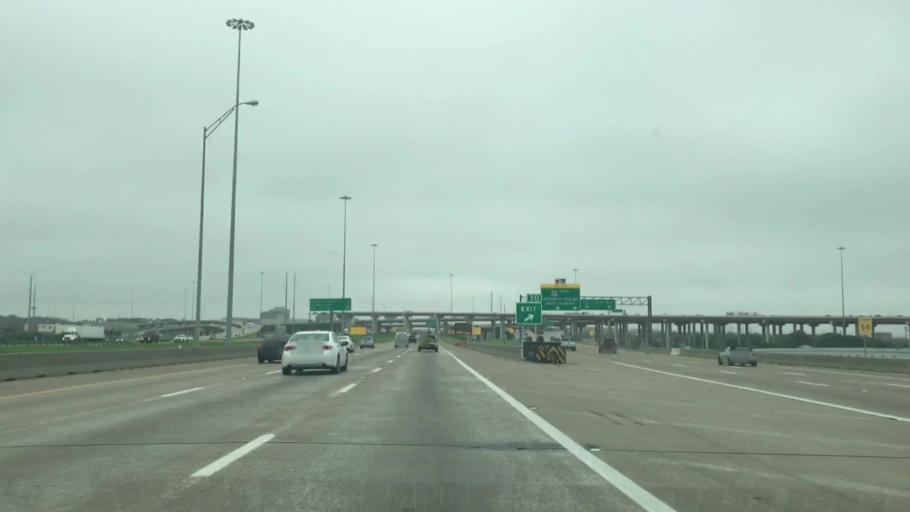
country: US
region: Texas
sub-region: Dallas County
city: Farmers Branch
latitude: 32.9104
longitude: -96.9351
